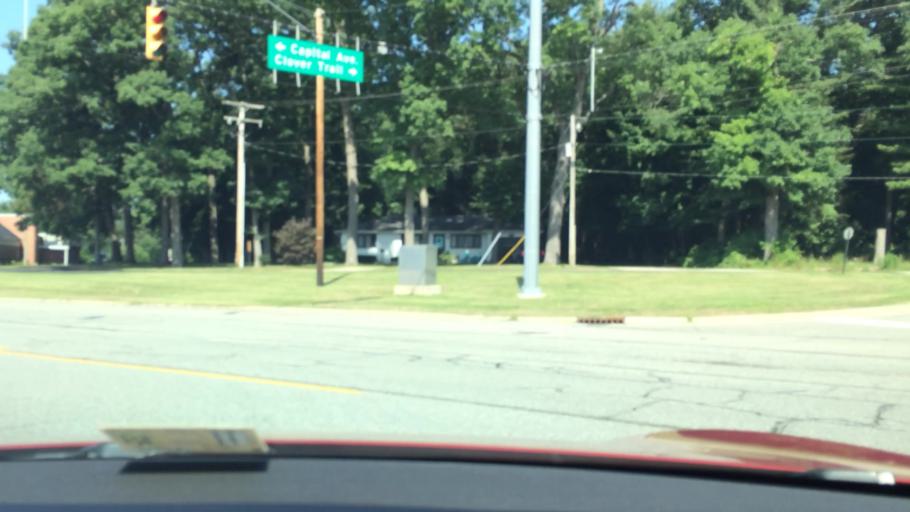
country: US
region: Indiana
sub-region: Saint Joseph County
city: Granger
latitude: 41.7366
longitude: -86.1522
